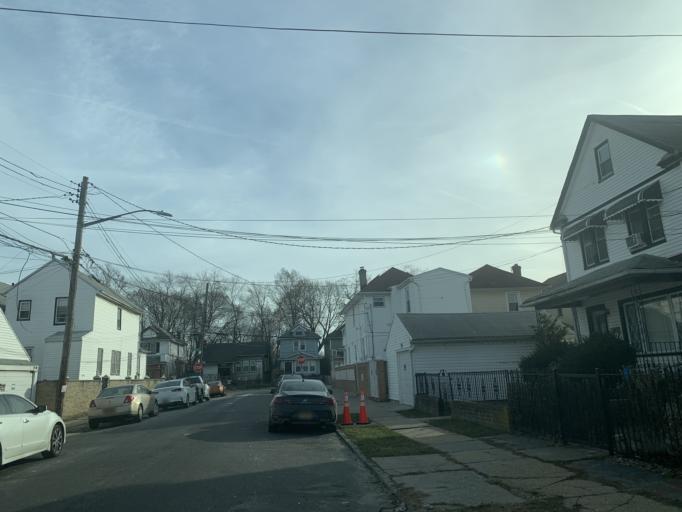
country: US
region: New York
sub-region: Queens County
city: Jamaica
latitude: 40.7029
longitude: -73.7881
